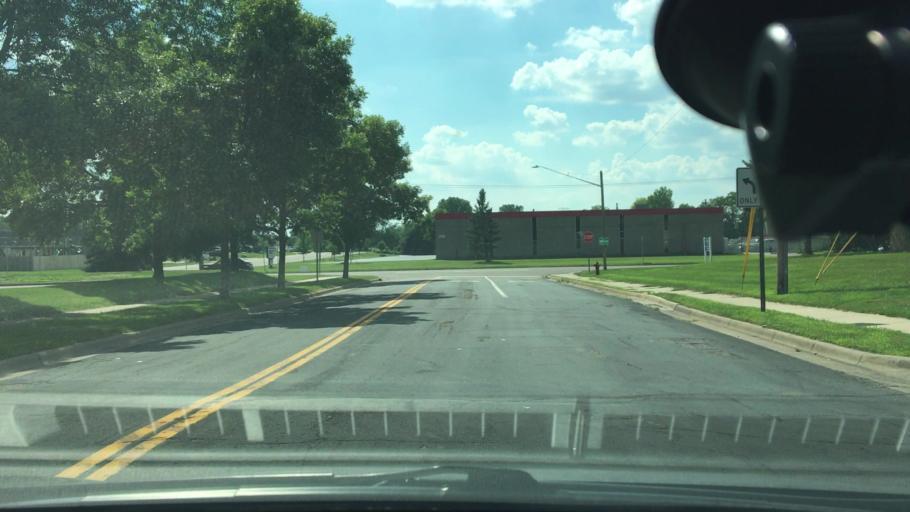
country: US
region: Minnesota
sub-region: Hennepin County
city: New Hope
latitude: 45.0548
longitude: -93.3897
